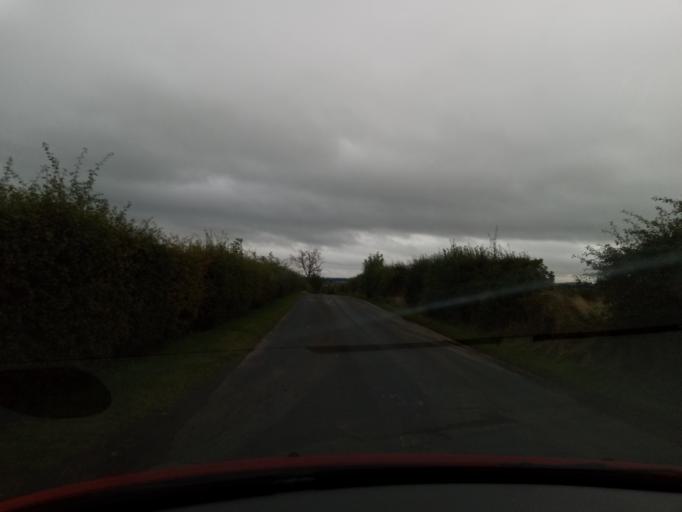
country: GB
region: Scotland
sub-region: The Scottish Borders
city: Saint Boswells
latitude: 55.5202
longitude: -2.6337
